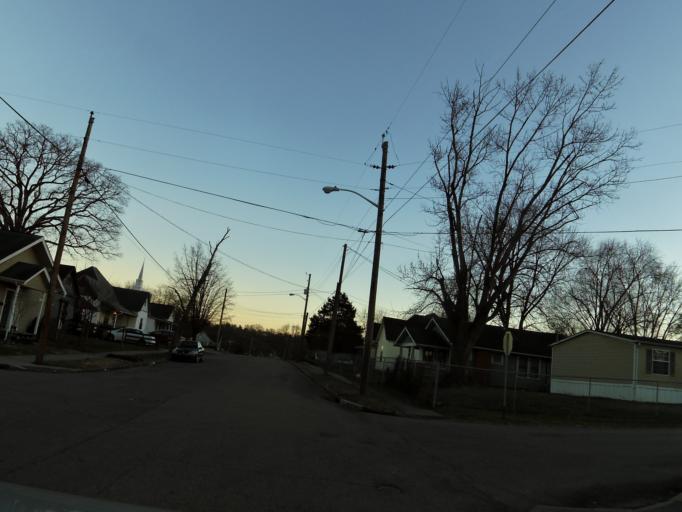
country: US
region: Tennessee
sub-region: Knox County
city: Knoxville
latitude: 35.9877
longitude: -83.9548
